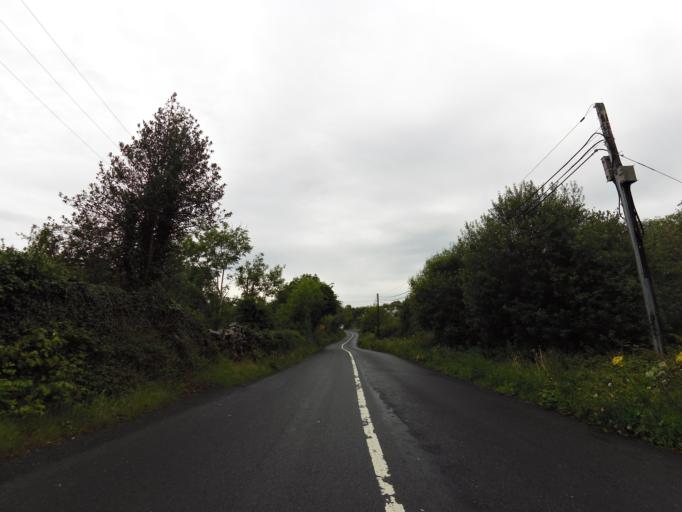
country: IE
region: Connaught
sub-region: County Galway
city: Gaillimh
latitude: 53.2981
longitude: -9.0557
